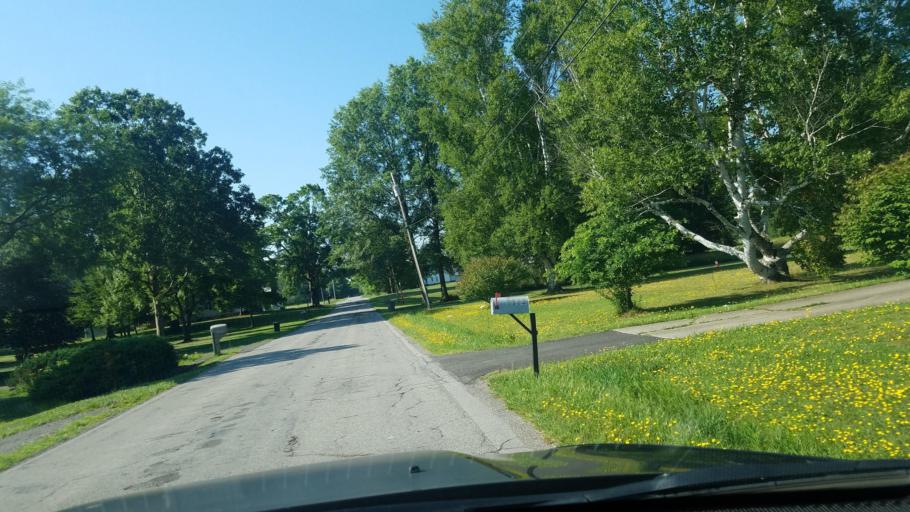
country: US
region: Ohio
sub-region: Trumbull County
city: Champion Heights
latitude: 41.3057
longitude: -80.8206
